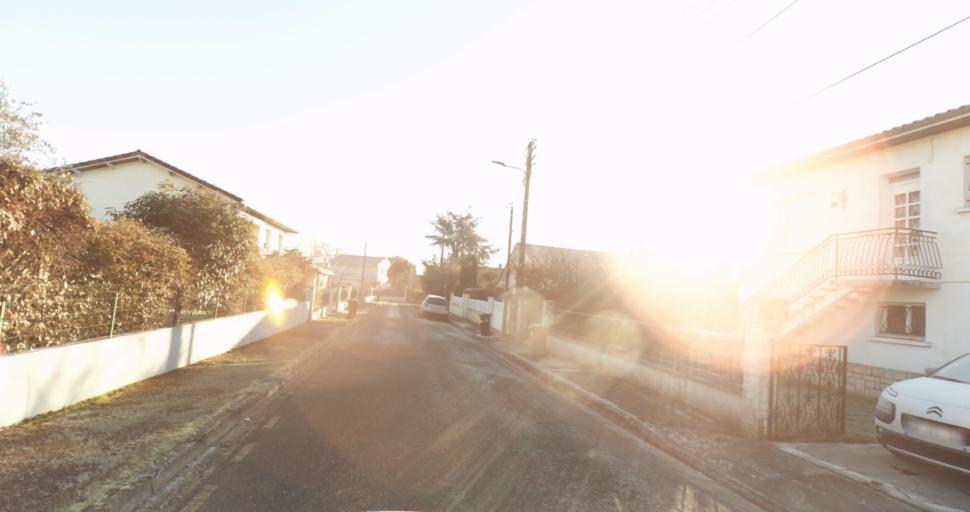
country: FR
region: Aquitaine
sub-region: Departement de la Gironde
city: Carbon-Blanc
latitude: 44.9070
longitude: -0.5006
